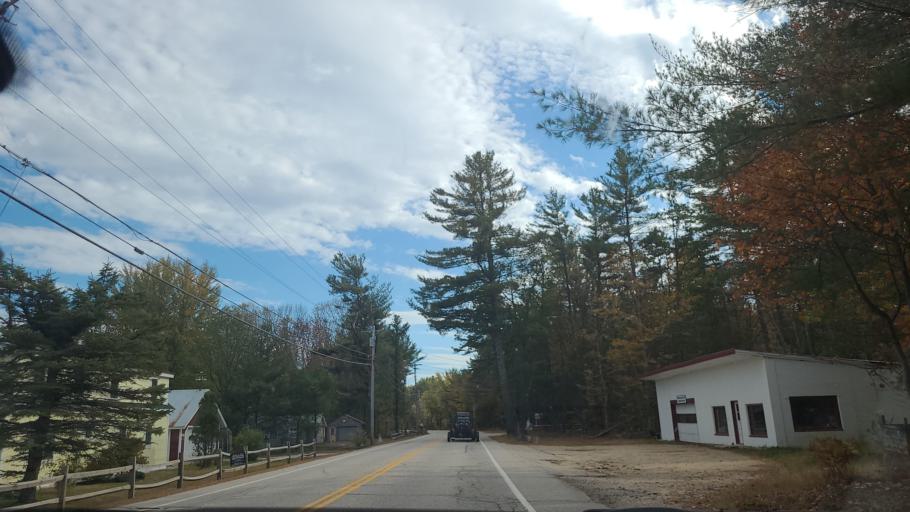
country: US
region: New Hampshire
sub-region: Carroll County
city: North Conway
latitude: 44.0264
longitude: -71.1334
